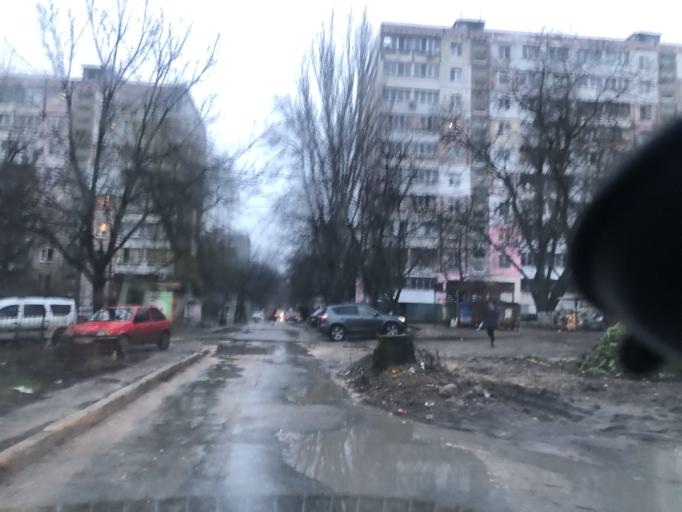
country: MD
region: Chisinau
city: Chisinau
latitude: 46.9858
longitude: 28.8543
